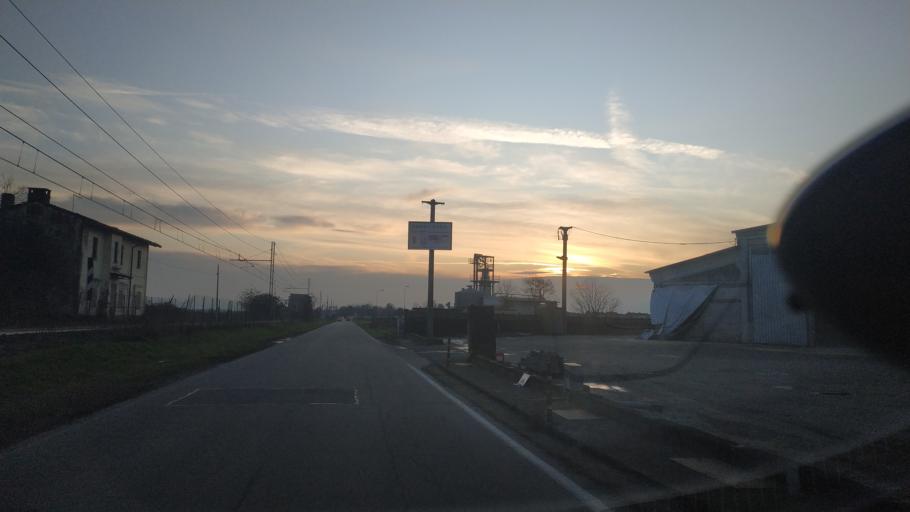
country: IT
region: Piedmont
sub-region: Provincia di Torino
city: Caluso
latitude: 45.2842
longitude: 7.8833
